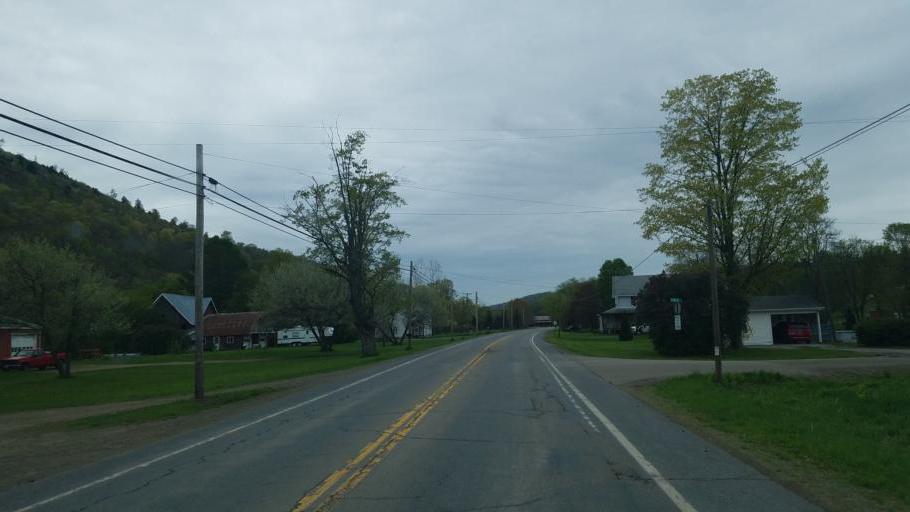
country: US
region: Pennsylvania
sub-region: Tioga County
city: Westfield
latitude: 41.9354
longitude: -77.6392
